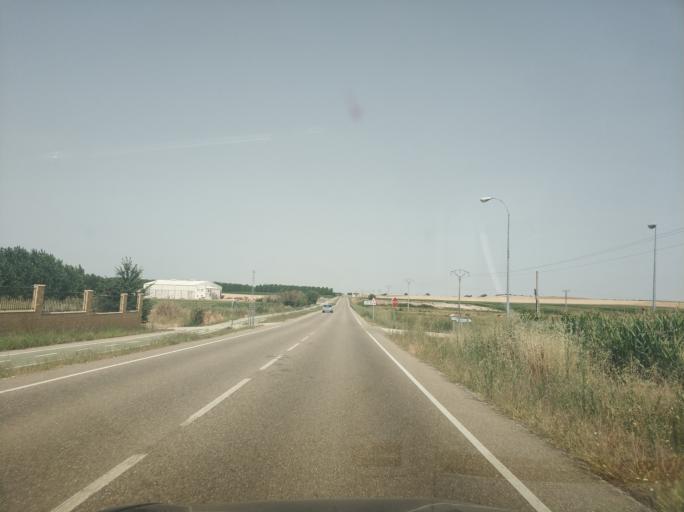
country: ES
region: Castille and Leon
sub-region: Provincia de Salamanca
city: Villamayor
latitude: 41.0194
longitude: -5.7179
